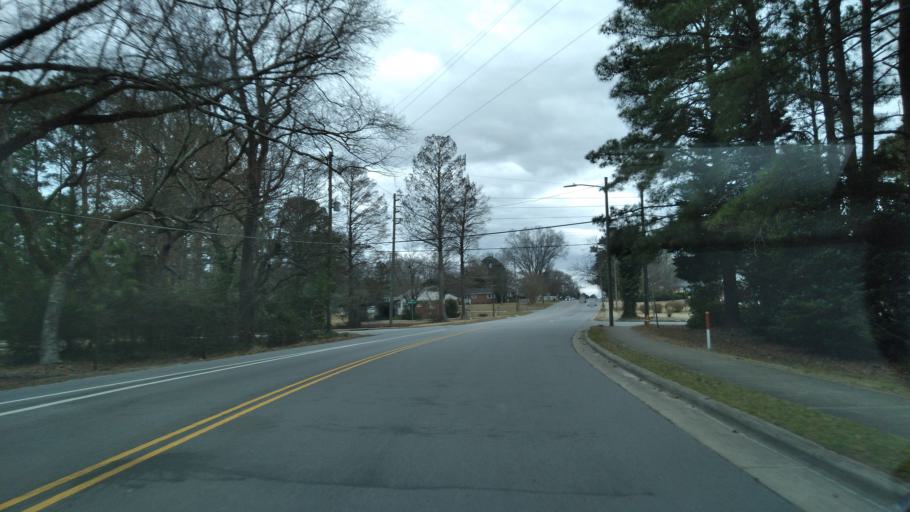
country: US
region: North Carolina
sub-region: Wake County
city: Garner
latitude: 35.7043
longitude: -78.6190
